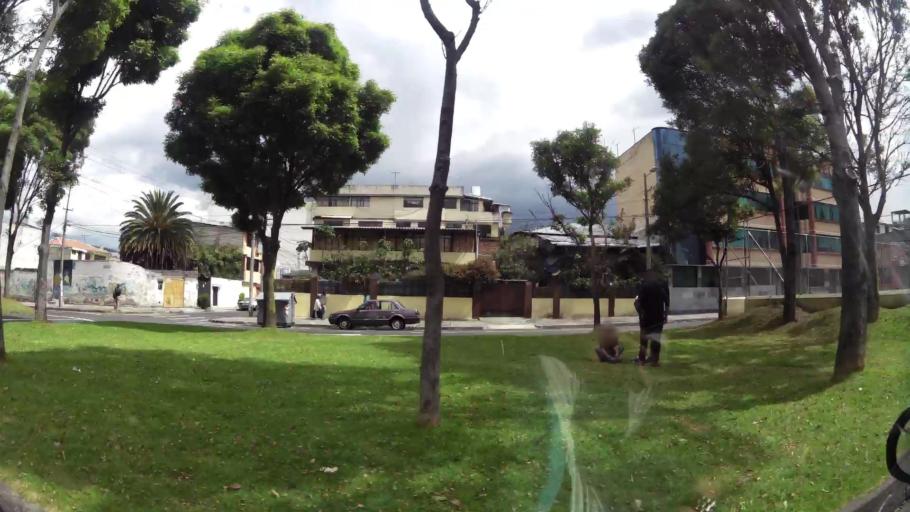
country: EC
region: Pichincha
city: Quito
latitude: -0.2477
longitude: -78.5316
